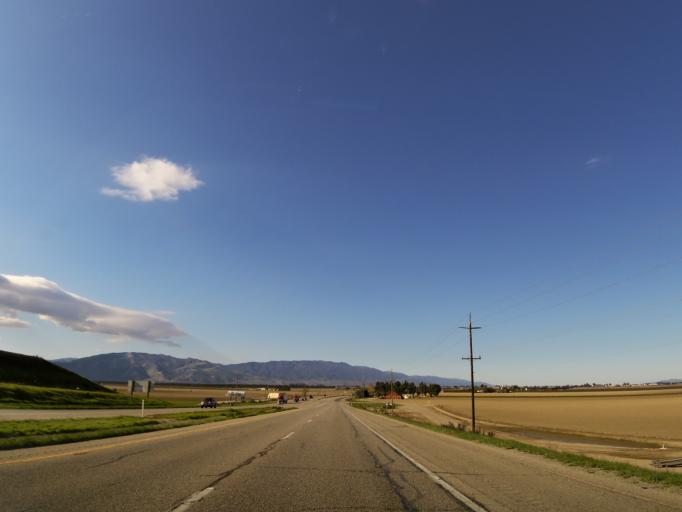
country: US
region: California
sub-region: Monterey County
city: Greenfield
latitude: 36.2972
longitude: -121.2108
